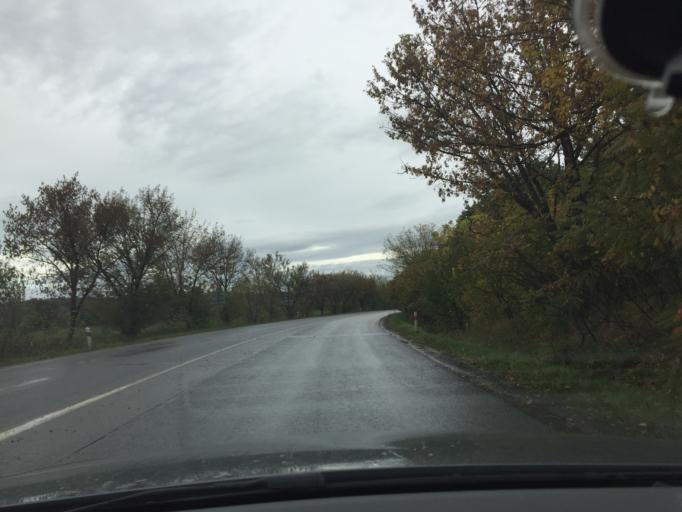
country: CZ
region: Central Bohemia
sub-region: Okres Melnik
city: Veltrusy
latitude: 50.2673
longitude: 14.3219
